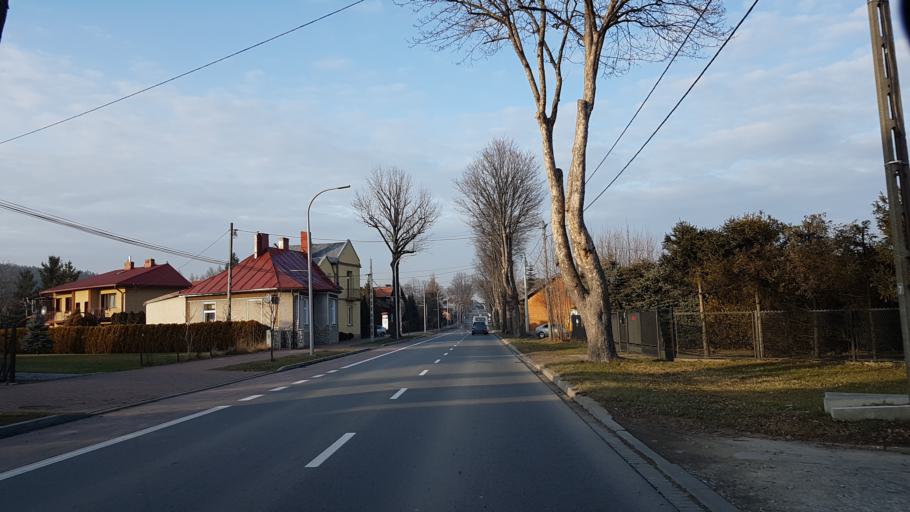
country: PL
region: Lesser Poland Voivodeship
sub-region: Powiat nowosadecki
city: Stary Sacz
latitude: 49.5531
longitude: 20.6396
